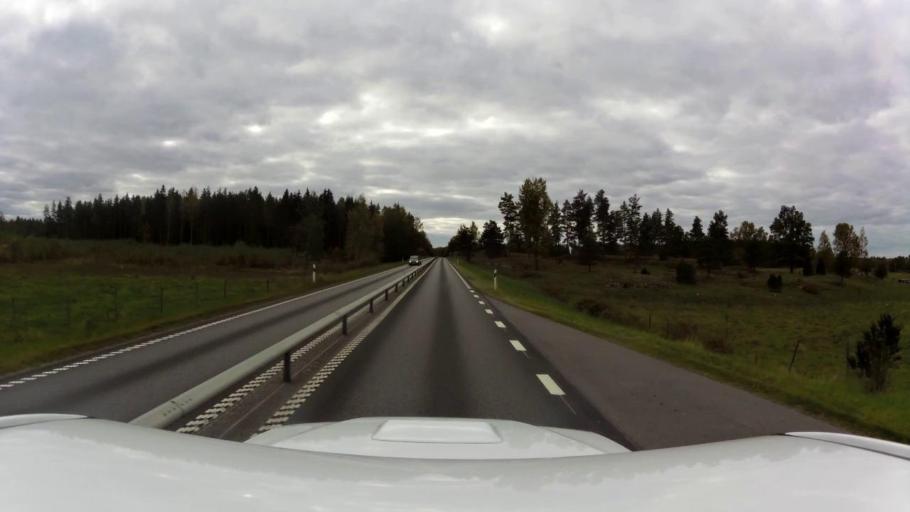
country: SE
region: OEstergoetland
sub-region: Linkopings Kommun
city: Malmslatt
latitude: 58.3002
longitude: 15.5639
